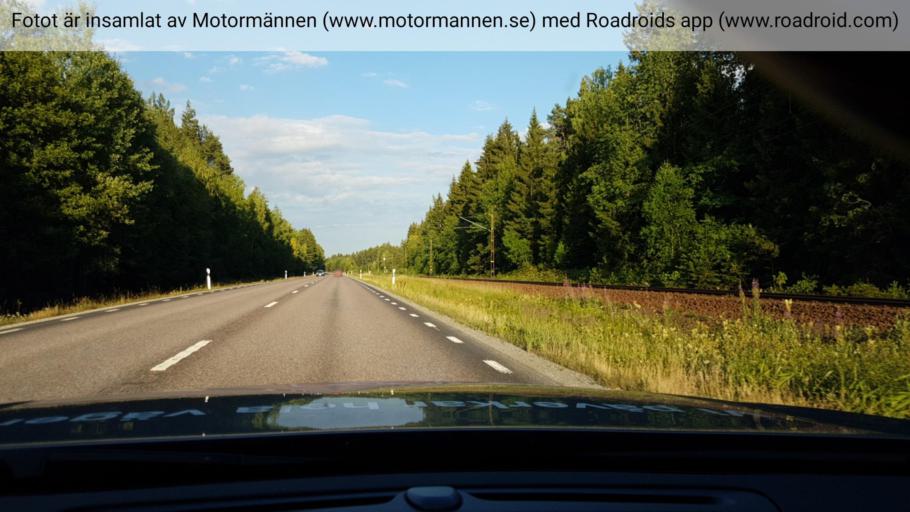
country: SE
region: Uppsala
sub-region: Enkopings Kommun
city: Orsundsbro
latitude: 59.8823
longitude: 17.2268
